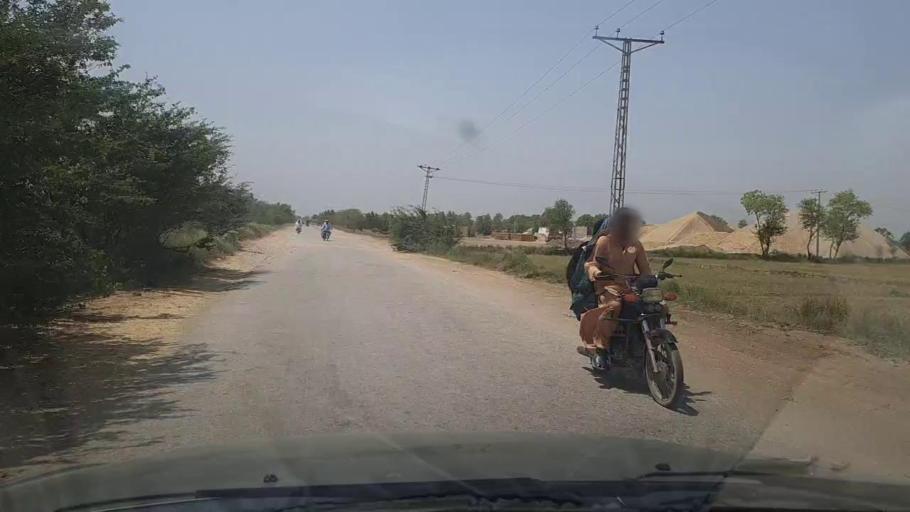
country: PK
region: Sindh
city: Karaundi
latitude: 26.8803
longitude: 68.3093
